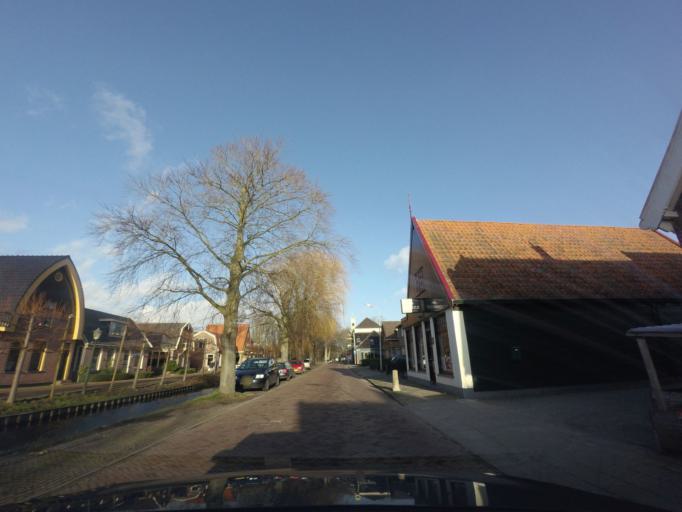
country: NL
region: North Holland
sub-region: Gemeente Opmeer
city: Opmeer
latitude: 52.7408
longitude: 4.8998
